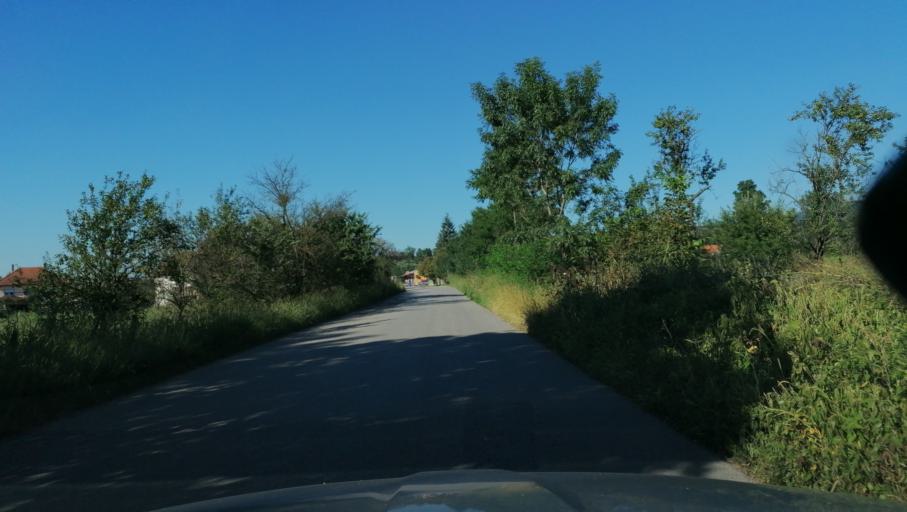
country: RS
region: Central Serbia
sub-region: Raski Okrug
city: Kraljevo
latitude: 43.8412
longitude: 20.5999
